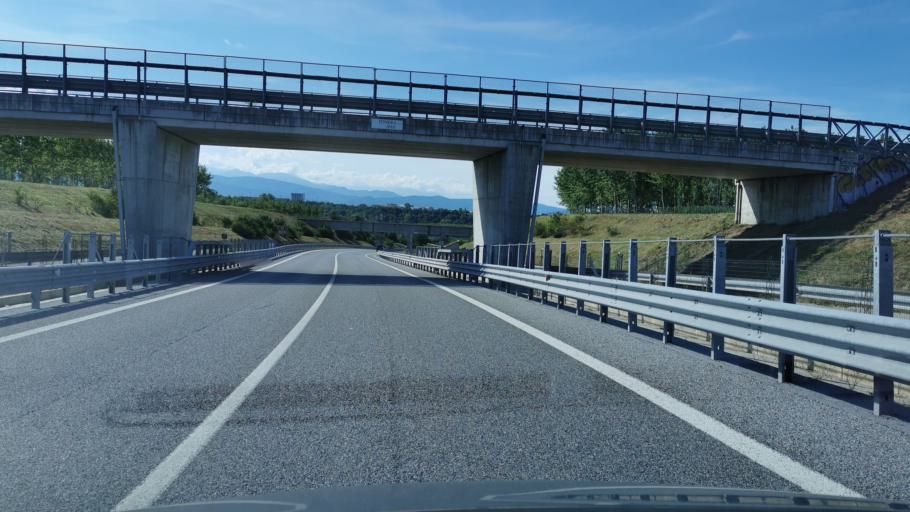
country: IT
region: Piedmont
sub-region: Provincia di Cuneo
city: Castelletto Stura
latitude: 44.4186
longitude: 7.5946
